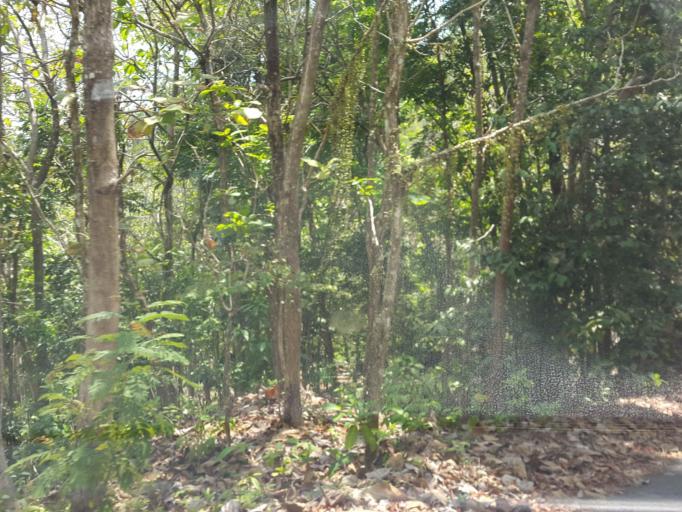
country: ID
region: East Java
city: Sudimoro
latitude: -8.2474
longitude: 111.2086
